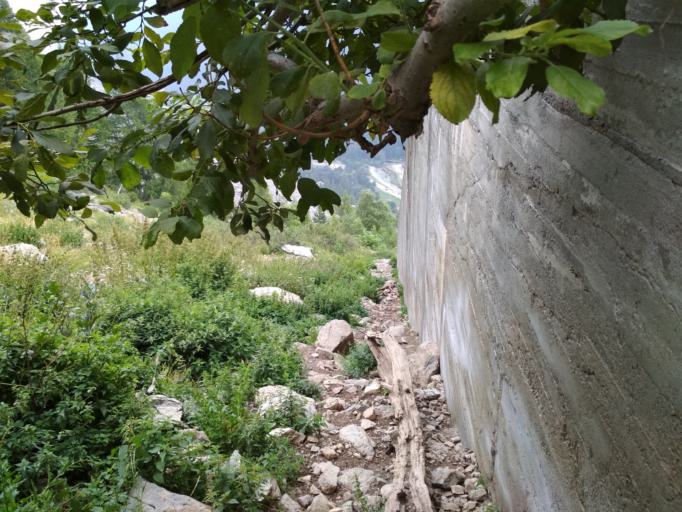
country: IT
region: Piedmont
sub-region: Provincia di Torino
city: Balme
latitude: 45.3057
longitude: 7.2157
